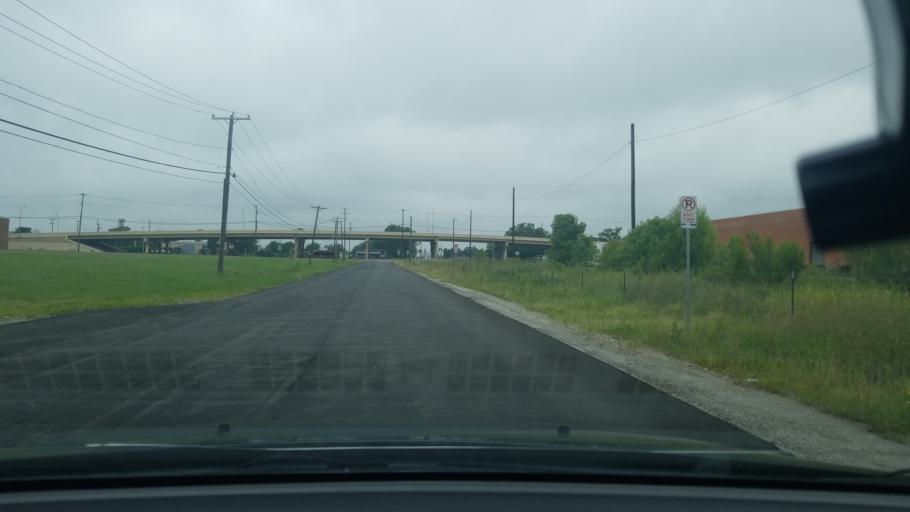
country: US
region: Texas
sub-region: Dallas County
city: Balch Springs
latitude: 32.7761
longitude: -96.6801
